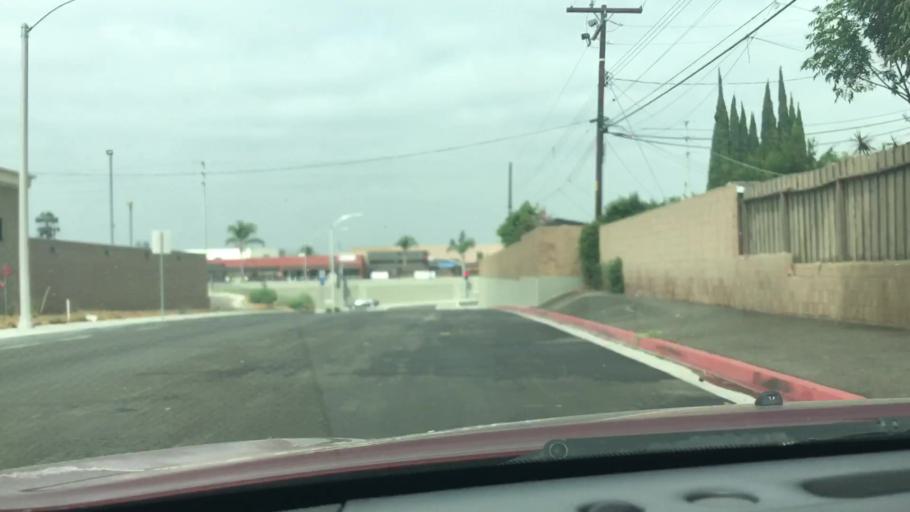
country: US
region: California
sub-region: Orange County
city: Placentia
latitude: 33.8682
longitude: -117.8883
